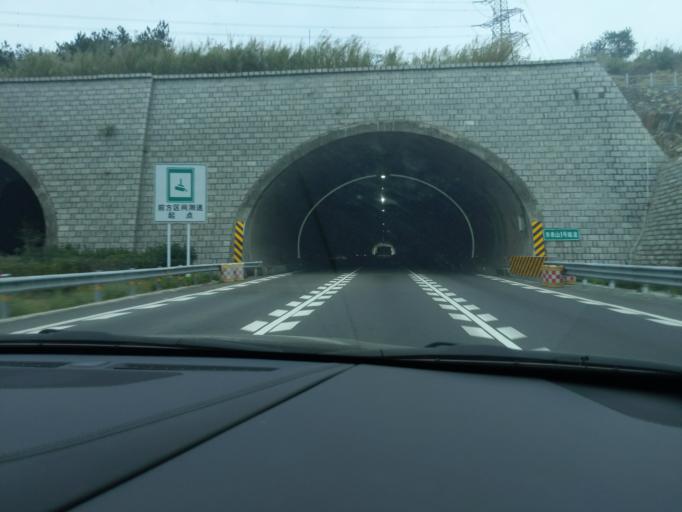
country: CN
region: Fujian
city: Cizao
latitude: 24.7766
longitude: 118.5106
